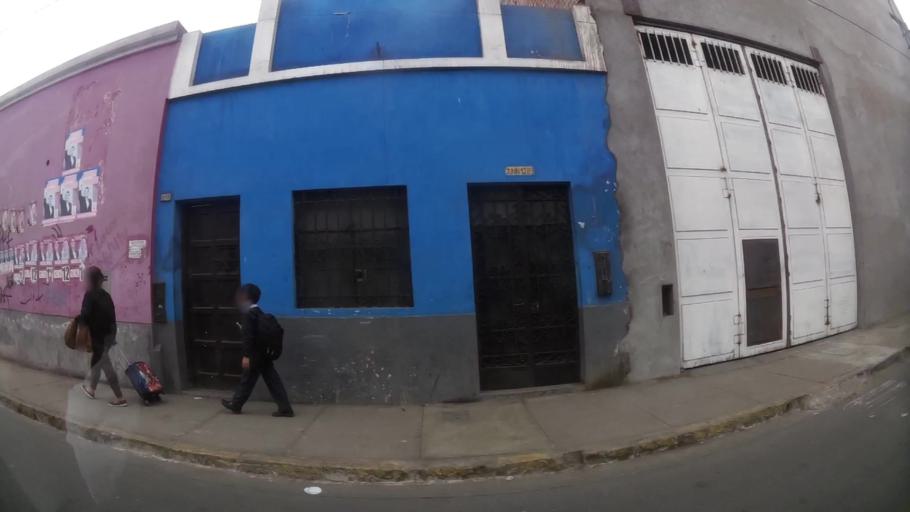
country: PE
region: Lima
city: Lima
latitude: -12.0514
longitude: -77.0168
